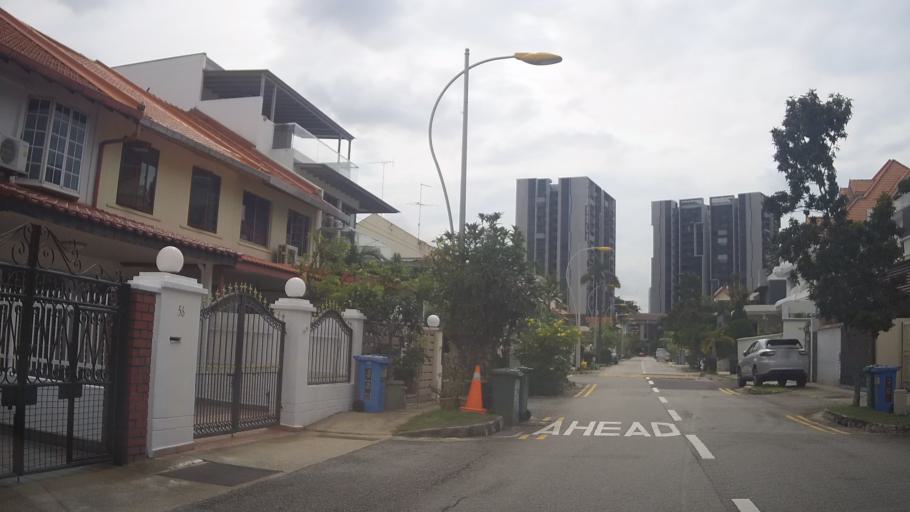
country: SG
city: Singapore
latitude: 1.3295
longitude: 103.8719
